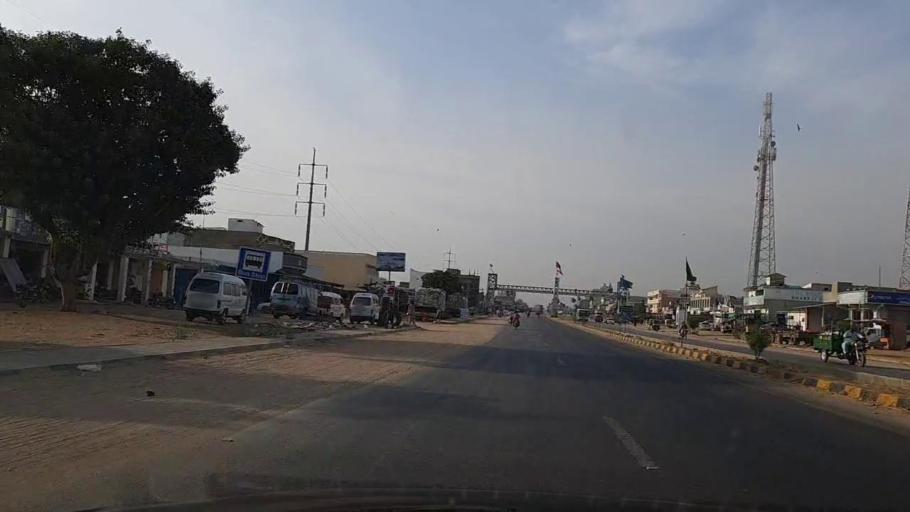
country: PK
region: Sindh
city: Gharo
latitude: 24.7885
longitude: 67.5279
